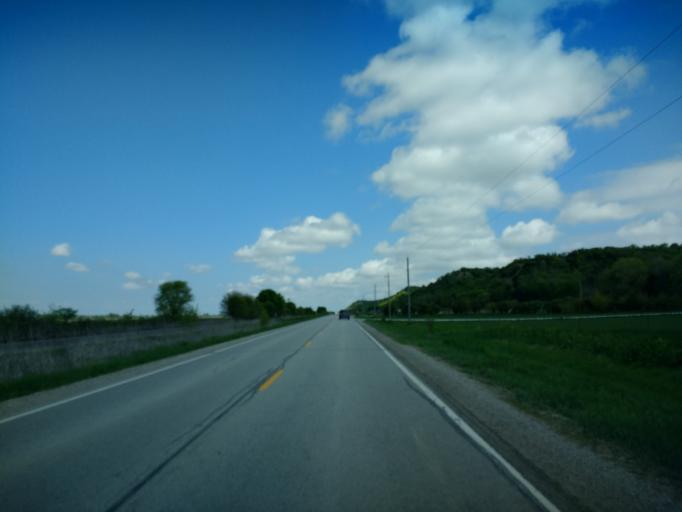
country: US
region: Iowa
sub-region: Harrison County
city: Missouri Valley
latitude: 41.4616
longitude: -95.8769
